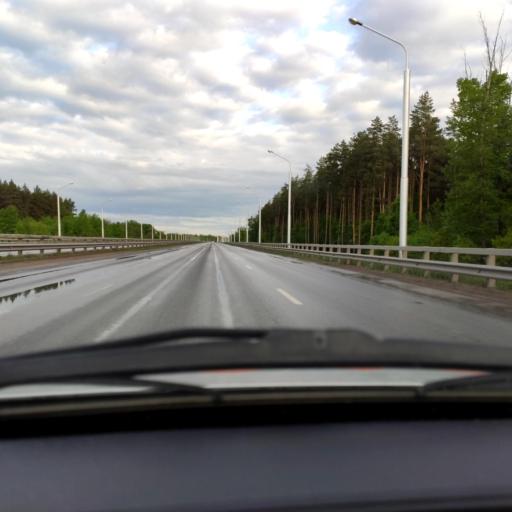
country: RU
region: Bashkortostan
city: Mikhaylovka
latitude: 54.7803
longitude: 55.9323
